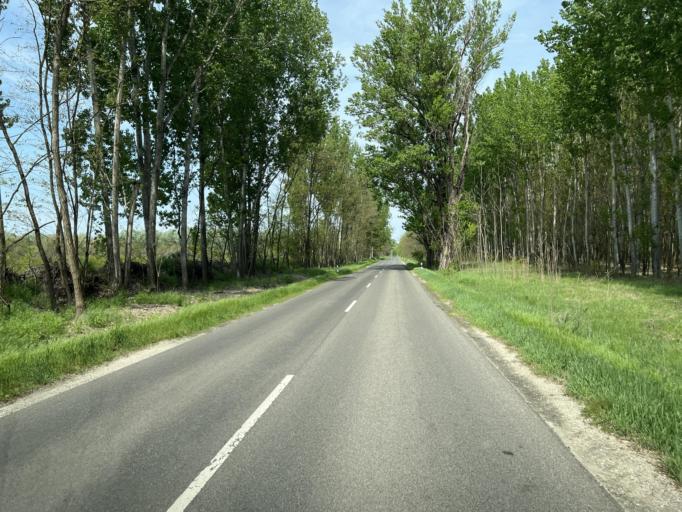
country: HU
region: Pest
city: Ujszilvas
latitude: 47.2545
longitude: 19.9421
